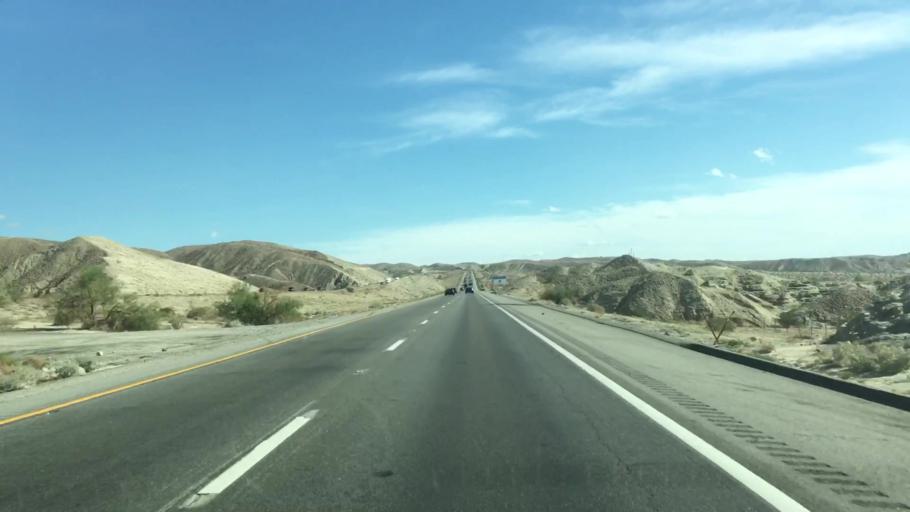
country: US
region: California
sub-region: Riverside County
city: Coachella
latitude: 33.7009
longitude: -116.1187
